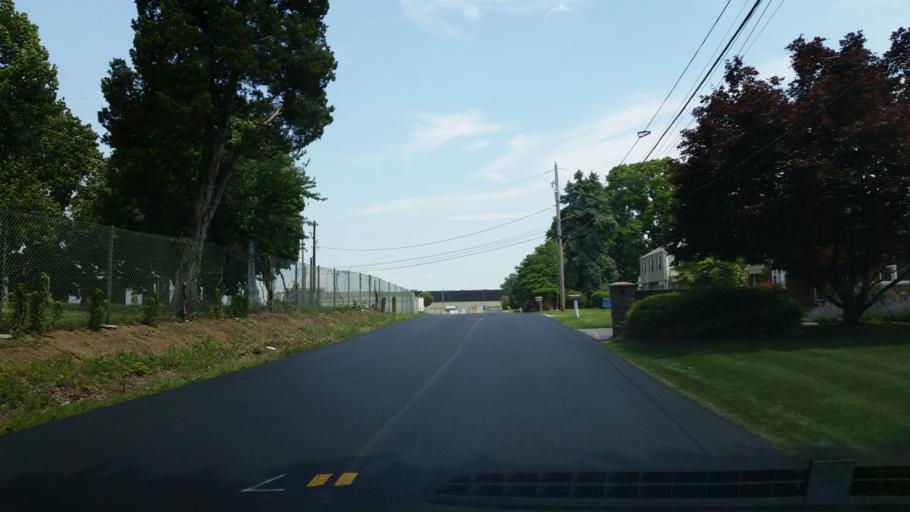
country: US
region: Pennsylvania
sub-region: Dauphin County
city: Steelton
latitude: 40.2124
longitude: -76.8560
